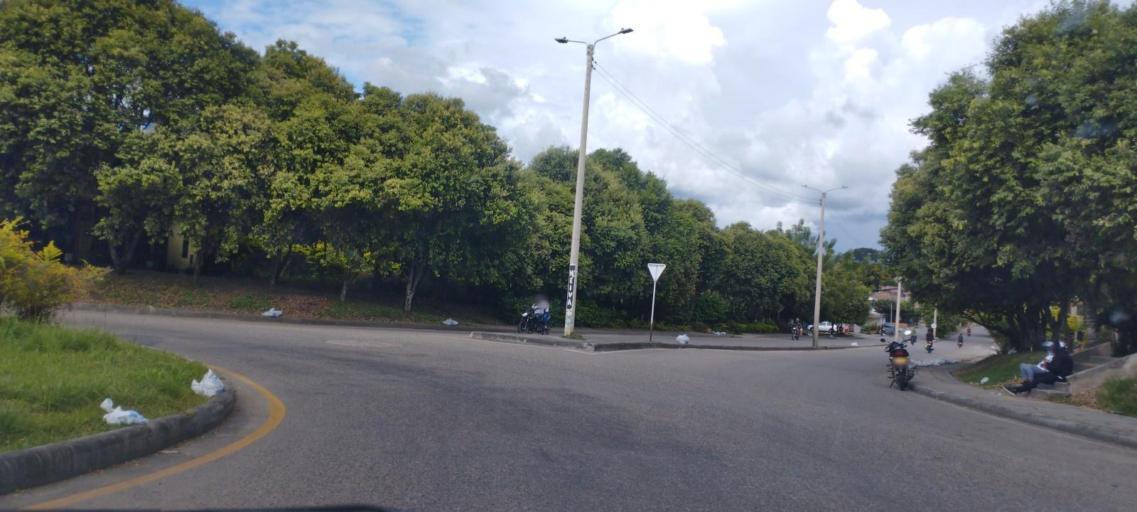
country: CO
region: Huila
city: Garzon
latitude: 2.1966
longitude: -75.6402
